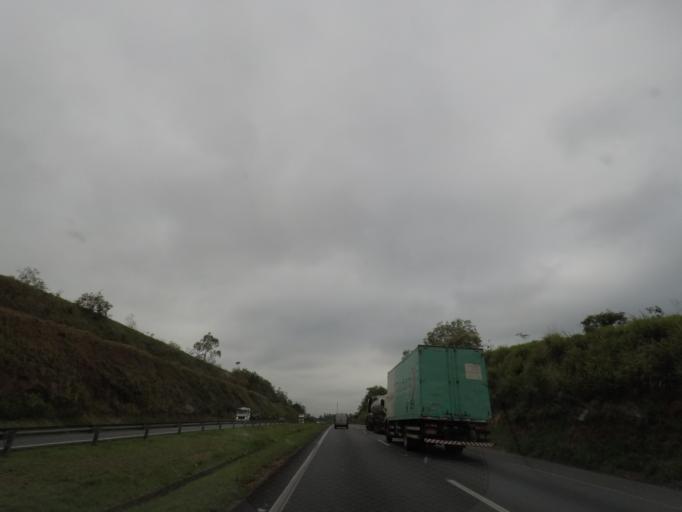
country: BR
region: Sao Paulo
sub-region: Itatiba
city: Itatiba
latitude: -22.9985
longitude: -46.7847
